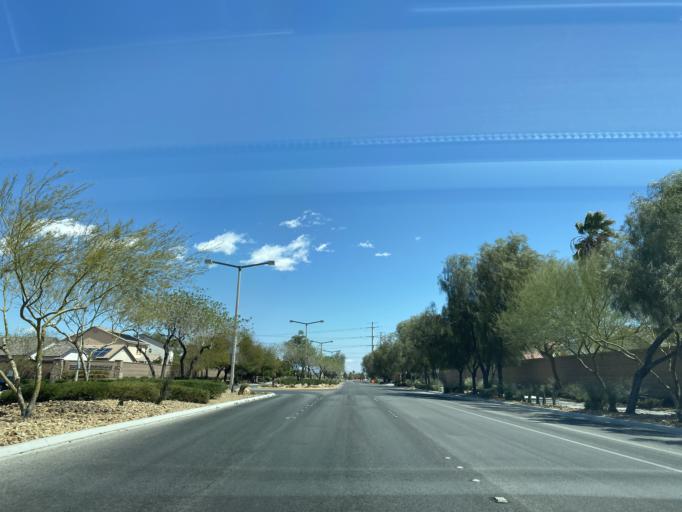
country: US
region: Nevada
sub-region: Clark County
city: North Las Vegas
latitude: 36.3058
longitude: -115.2111
